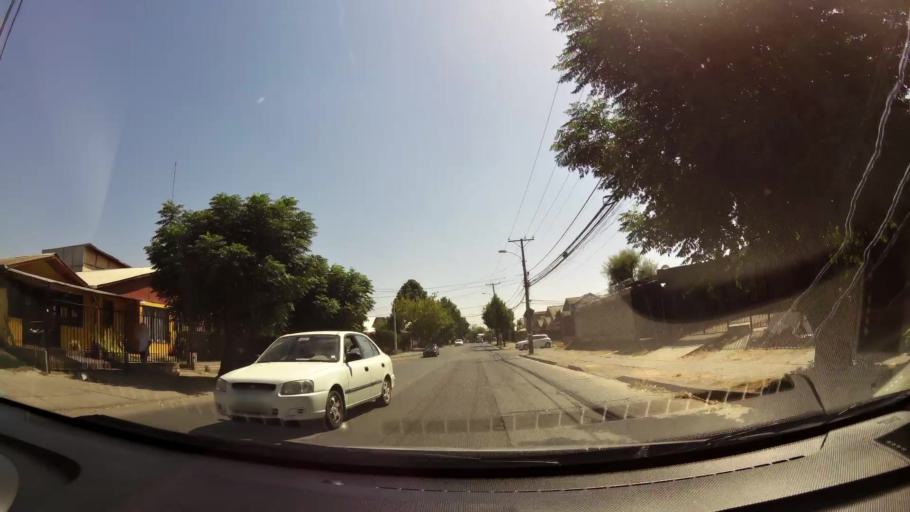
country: CL
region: Maule
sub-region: Provincia de Talca
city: Talca
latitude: -35.4201
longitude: -71.6444
